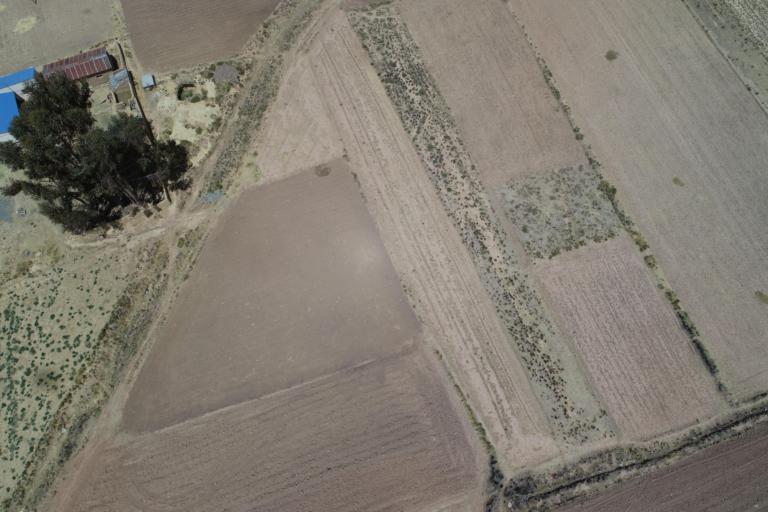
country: BO
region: La Paz
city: Achacachi
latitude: -15.9143
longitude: -68.8875
